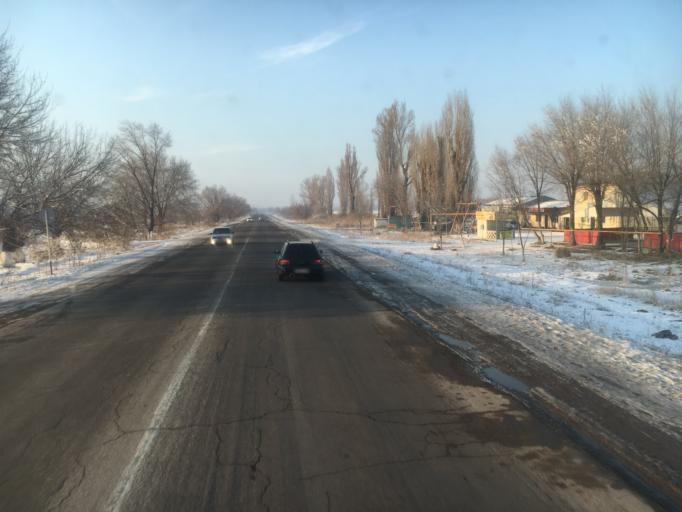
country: KZ
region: Almaty Oblysy
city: Burunday
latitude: 43.3427
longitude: 76.6570
